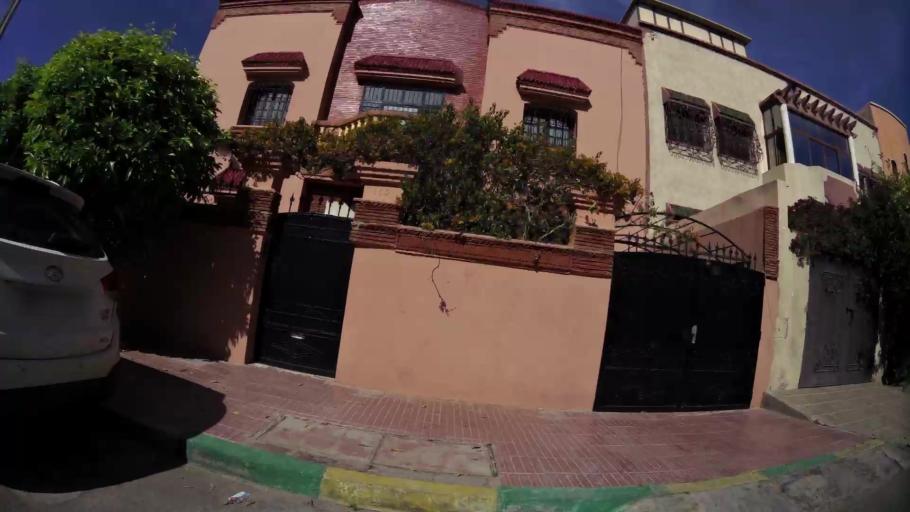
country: MA
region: Marrakech-Tensift-Al Haouz
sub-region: Marrakech
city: Marrakesh
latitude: 31.6491
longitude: -8.0489
